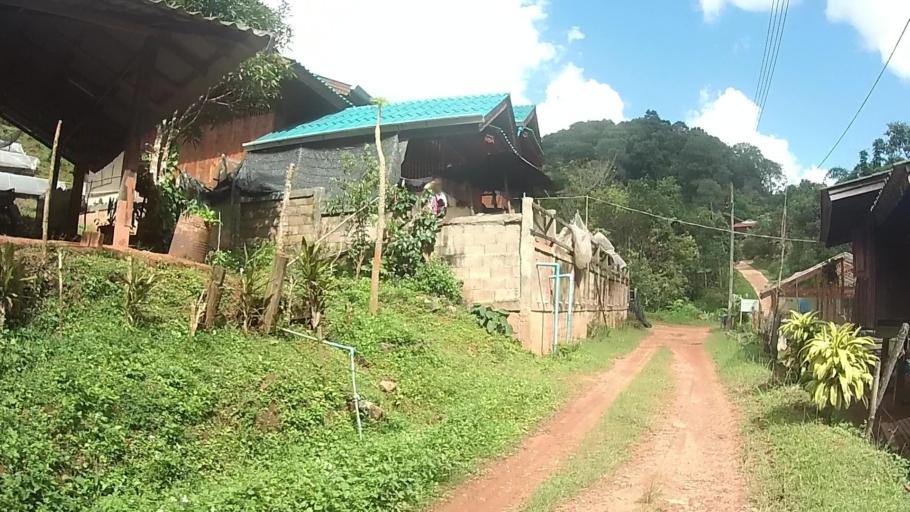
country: TH
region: Lampang
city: Mueang Pan
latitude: 18.9778
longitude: 99.4325
